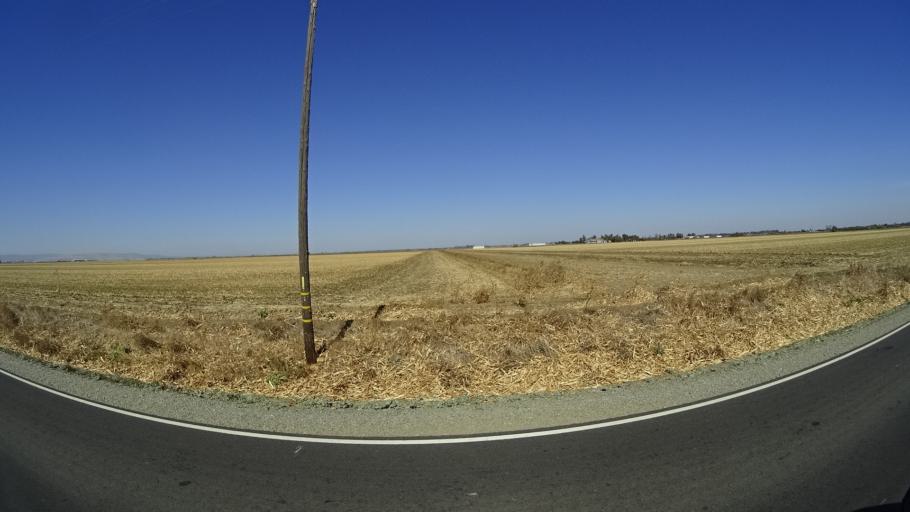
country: US
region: California
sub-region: Yolo County
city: Cottonwood
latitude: 38.6199
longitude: -121.9004
